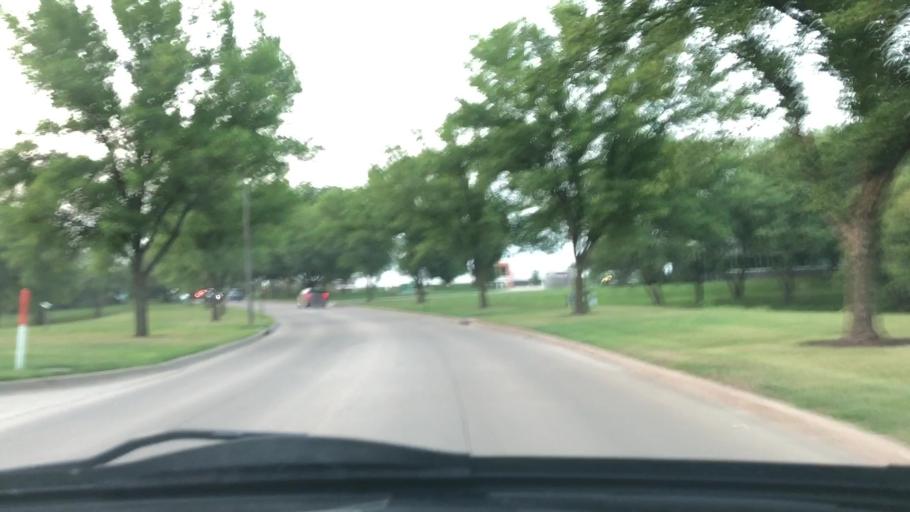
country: US
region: Iowa
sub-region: Johnson County
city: North Liberty
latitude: 41.7117
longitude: -91.6049
